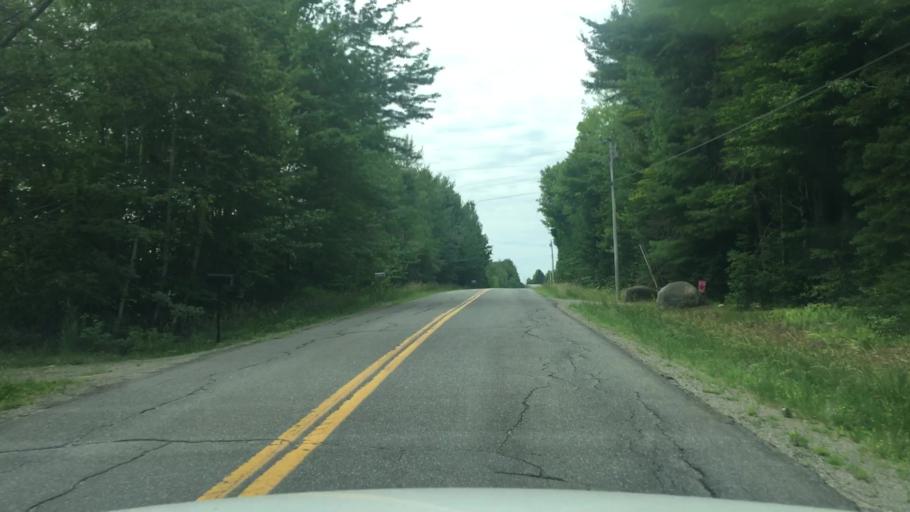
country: US
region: Maine
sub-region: Kennebec County
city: Albion
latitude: 44.5006
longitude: -69.3650
